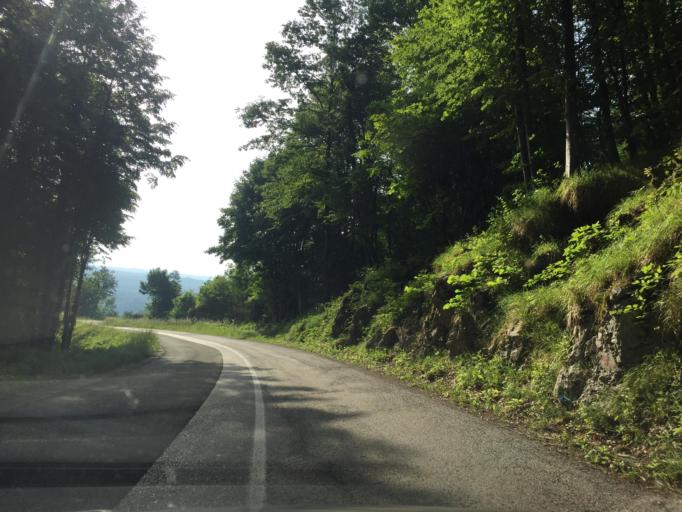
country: HR
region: Primorsko-Goranska
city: Matulji
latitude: 45.4064
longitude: 14.2616
